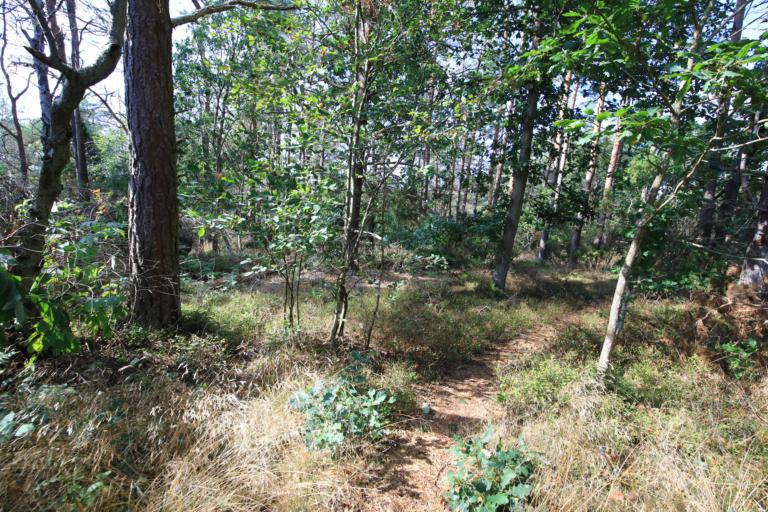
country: SE
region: Halland
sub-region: Varbergs Kommun
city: Varberg
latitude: 57.1750
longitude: 12.2189
